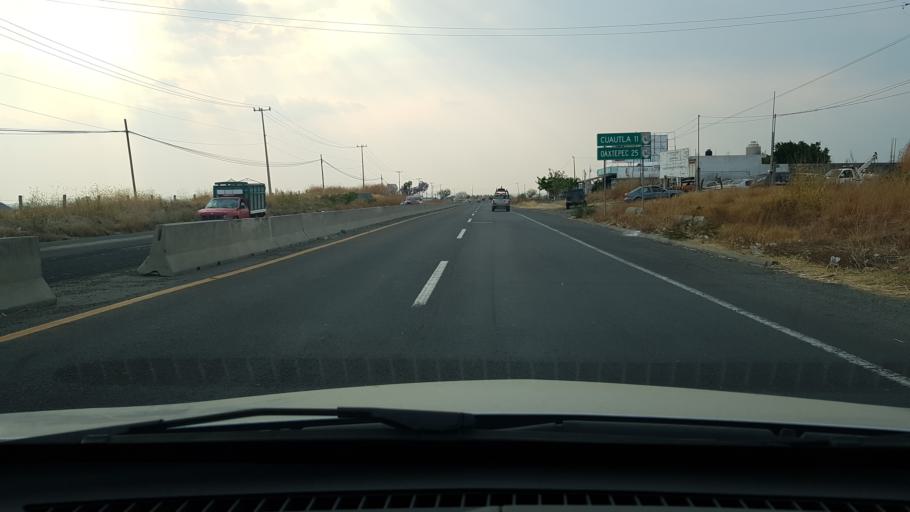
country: MX
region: Morelos
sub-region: Ayala
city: Unidad Habitacional Mariano Matamoros
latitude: 18.7535
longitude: -98.8569
